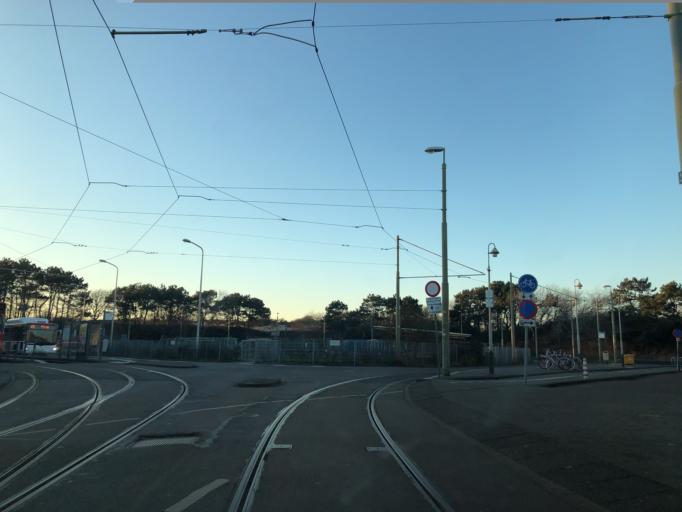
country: NL
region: South Holland
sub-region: Gemeente Den Haag
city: Scheveningen
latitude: 52.0875
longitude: 4.2529
